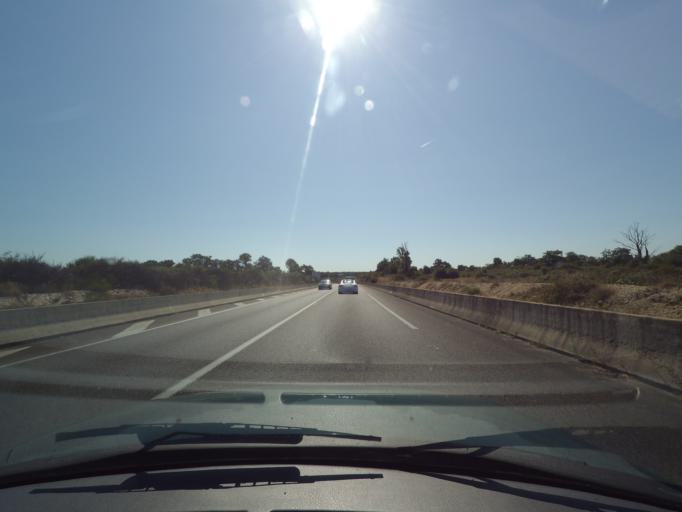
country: FR
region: Limousin
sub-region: Departement de la Haute-Vienne
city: Peyrat-de-Bellac
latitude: 46.1383
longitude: 1.0568
